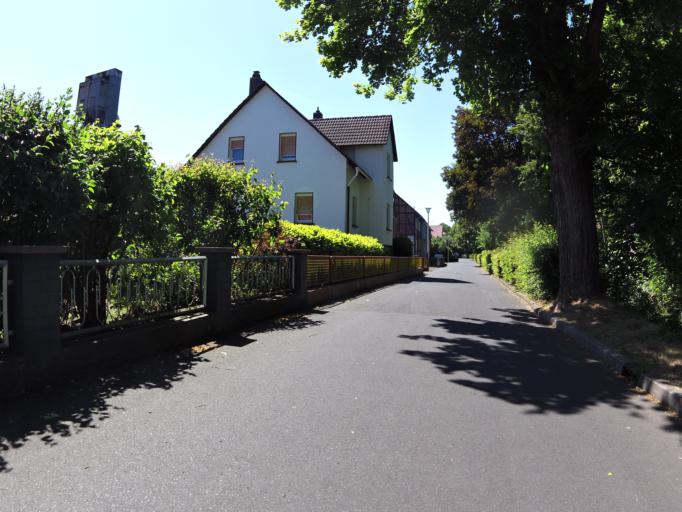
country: DE
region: Thuringia
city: Dankmarshausen
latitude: 50.9494
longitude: 10.0303
